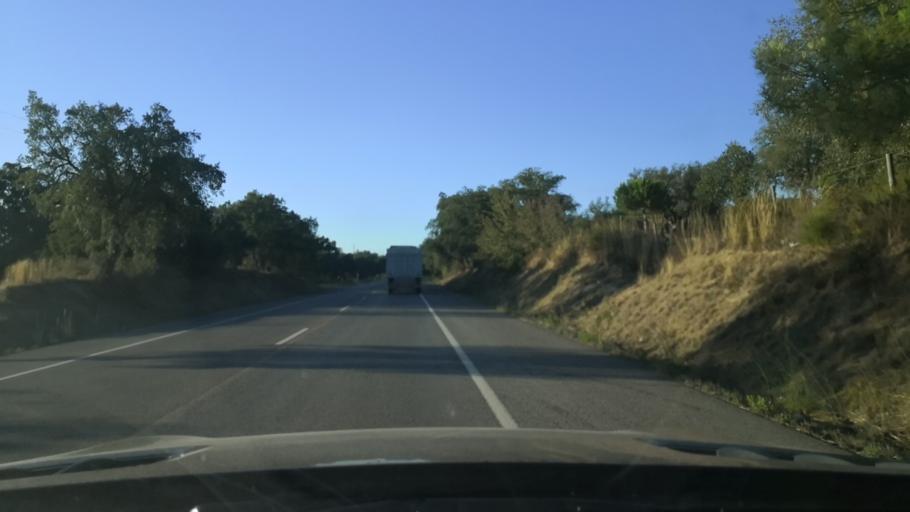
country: PT
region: Setubal
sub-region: Alcacer do Sal
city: Alcacer do Sal
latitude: 38.4920
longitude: -8.5999
